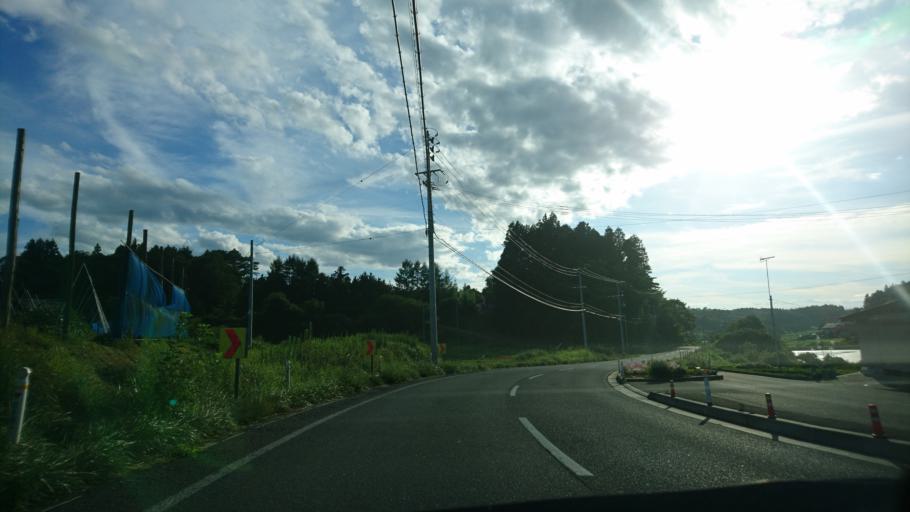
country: JP
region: Iwate
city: Ichinoseki
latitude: 38.8668
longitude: 141.1956
